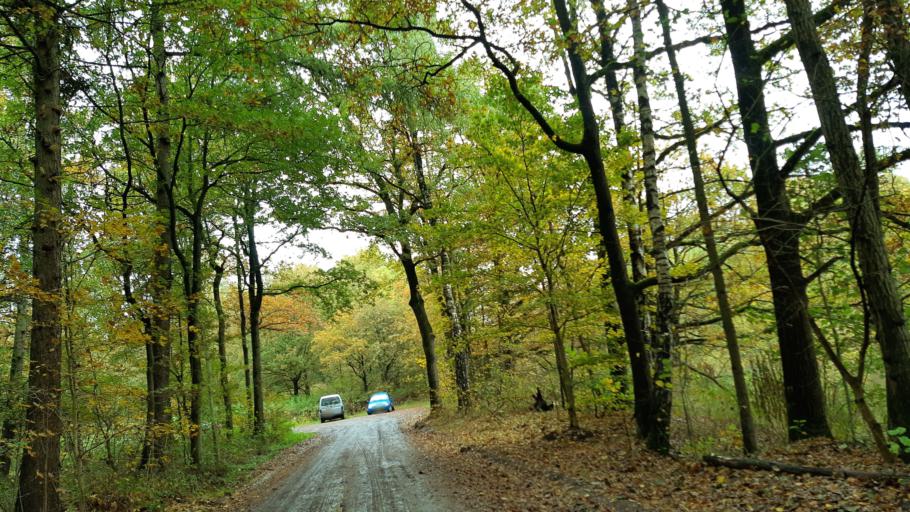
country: NL
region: Friesland
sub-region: Gemeente Lemsterland
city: Echtenerbrug
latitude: 52.7733
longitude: 5.8273
